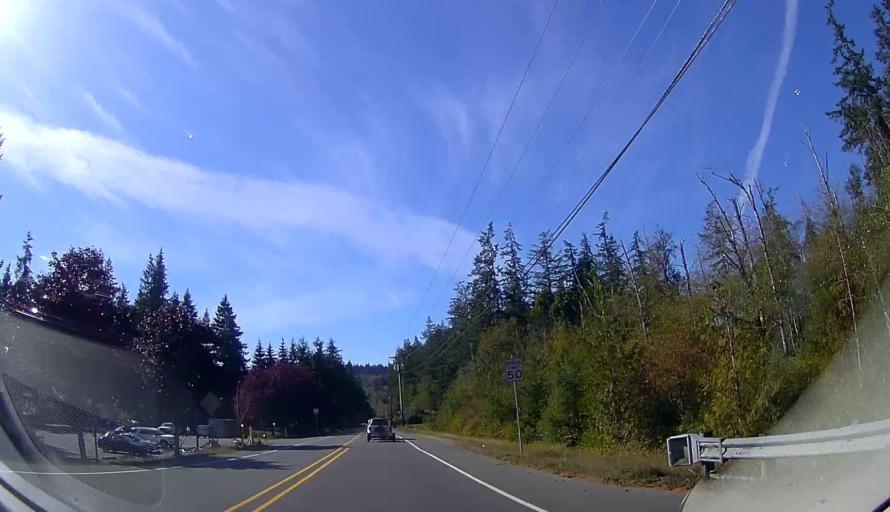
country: US
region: Washington
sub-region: Island County
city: Camano
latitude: 48.2318
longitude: -122.4735
